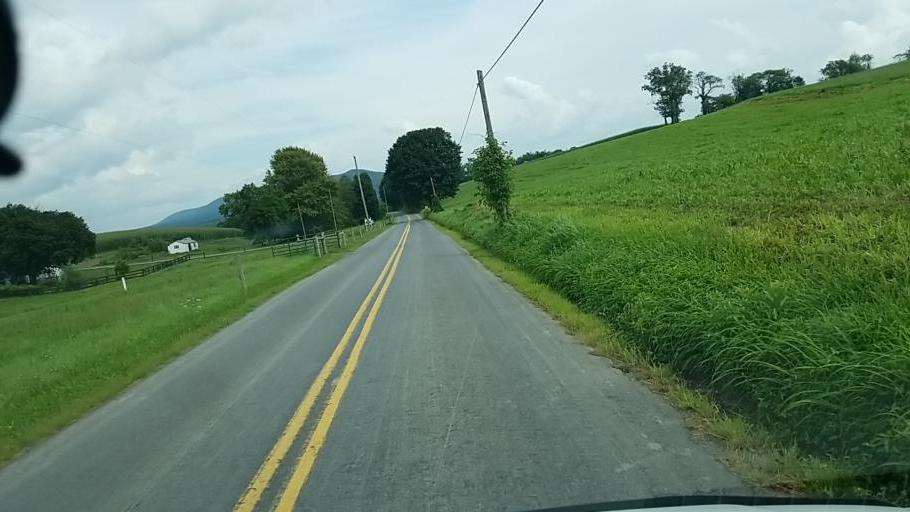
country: US
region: Pennsylvania
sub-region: Dauphin County
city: Elizabethville
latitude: 40.5800
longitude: -76.8090
